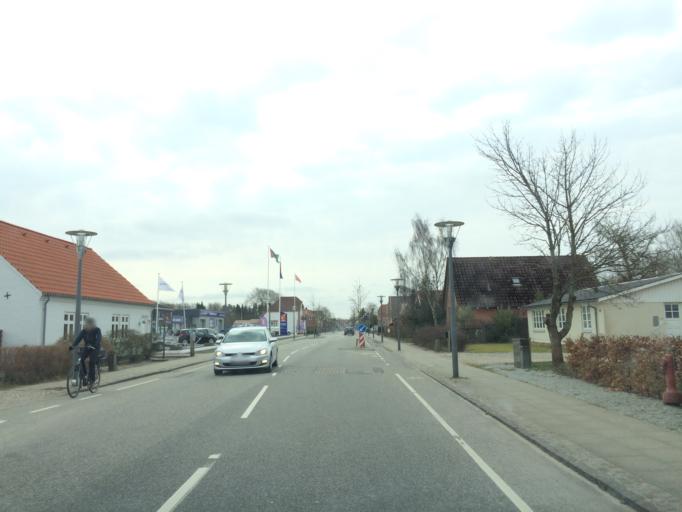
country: DK
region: Central Jutland
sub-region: Ringkobing-Skjern Kommune
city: Tarm
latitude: 55.9141
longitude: 8.5192
